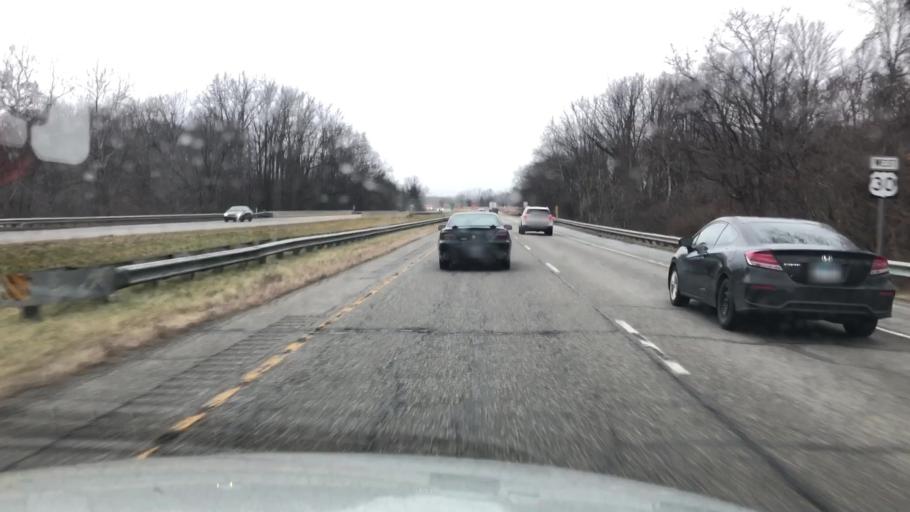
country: US
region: Indiana
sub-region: Marshall County
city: Plymouth
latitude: 41.3541
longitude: -86.2798
